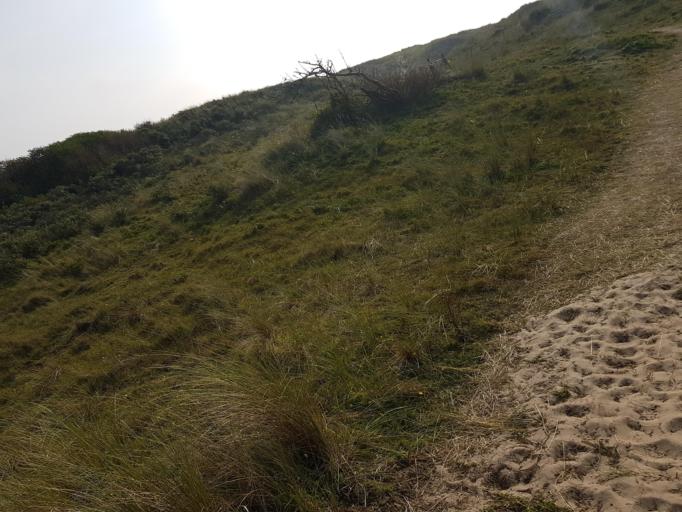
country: NL
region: North Holland
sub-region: Gemeente Texel
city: Den Burg
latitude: 53.1413
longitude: 4.8059
